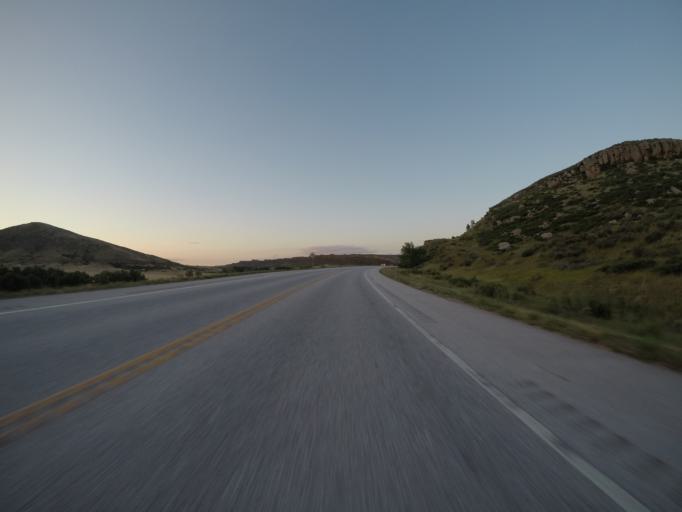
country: US
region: Colorado
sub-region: Larimer County
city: Laporte
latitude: 40.6724
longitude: -105.1900
